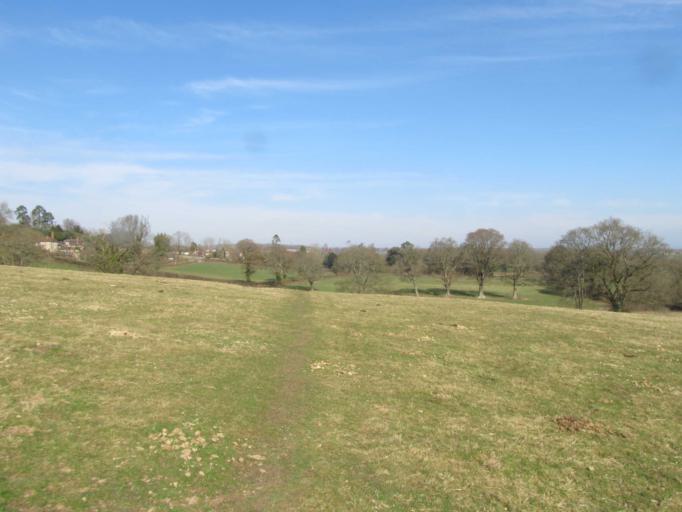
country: GB
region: England
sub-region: West Sussex
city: Petworth
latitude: 50.9886
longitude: -0.6067
